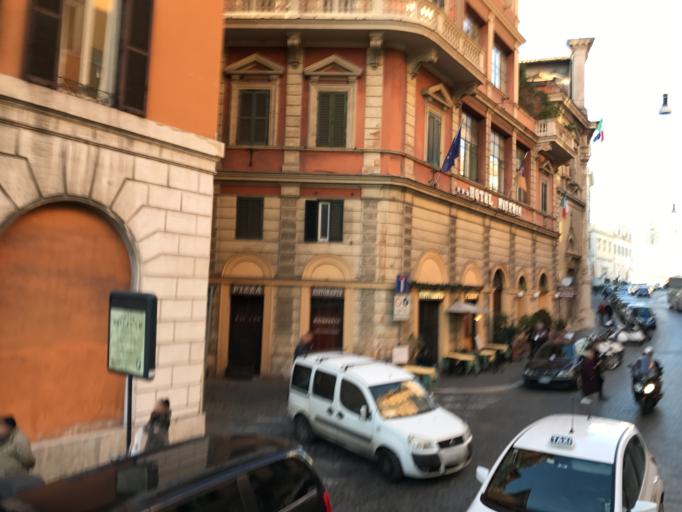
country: IT
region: Latium
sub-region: Citta metropolitana di Roma Capitale
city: Rome
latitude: 41.8970
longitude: 12.4869
